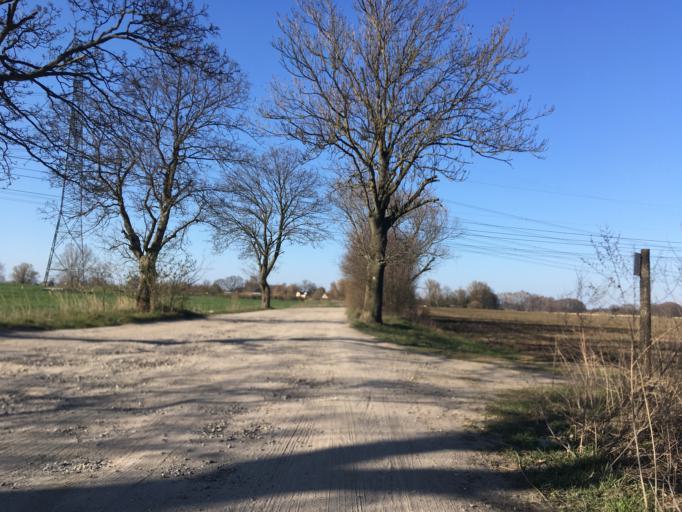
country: DE
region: Brandenburg
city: Ahrensfelde
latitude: 52.6198
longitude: 13.5736
